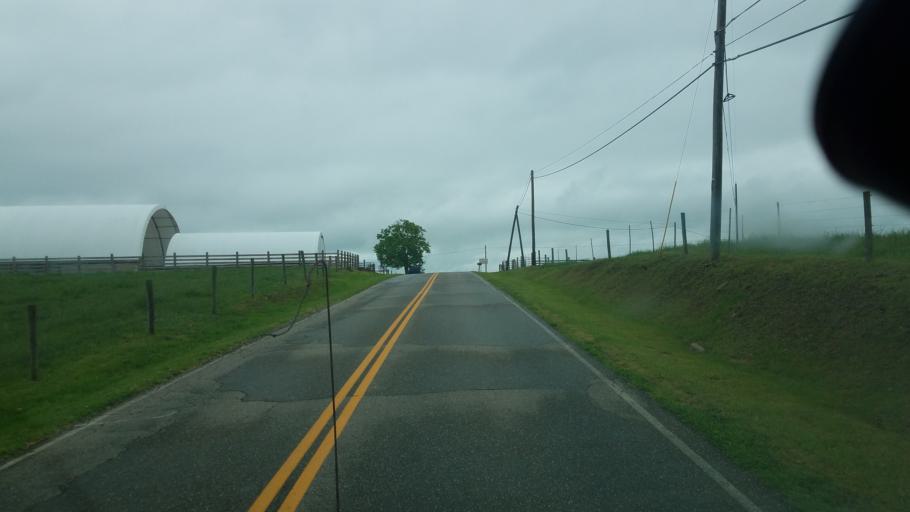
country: US
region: Ohio
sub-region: Jefferson County
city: Tiltonsville
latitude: 40.2234
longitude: -80.7198
